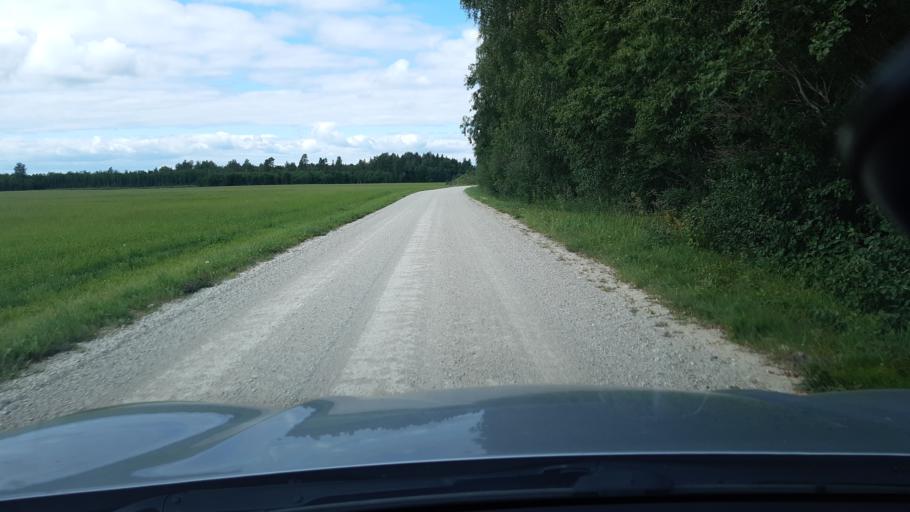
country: EE
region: Paernumaa
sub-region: Vaendra vald (alev)
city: Vandra
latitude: 58.7850
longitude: 25.0333
